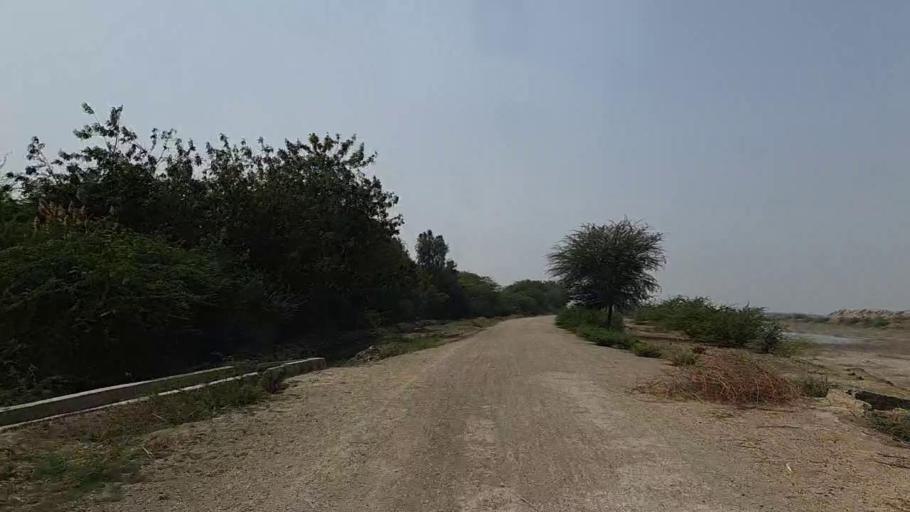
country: PK
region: Sindh
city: Naukot
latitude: 24.7952
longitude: 69.3481
